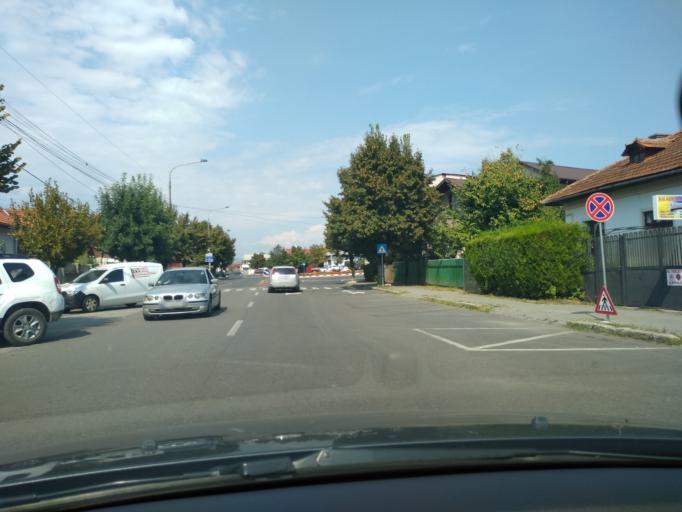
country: RO
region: Gorj
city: Targu Jiu
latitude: 45.0441
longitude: 23.2720
